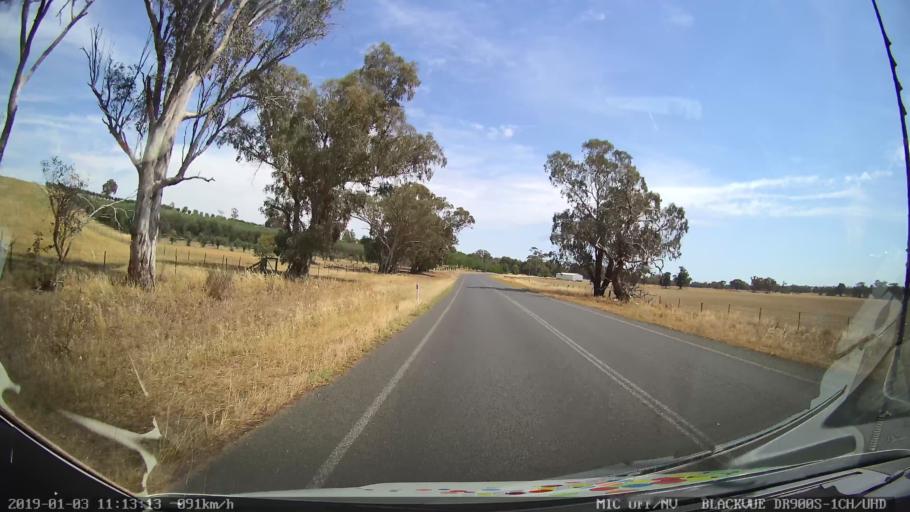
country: AU
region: New South Wales
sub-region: Young
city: Young
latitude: -34.1915
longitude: 148.2611
